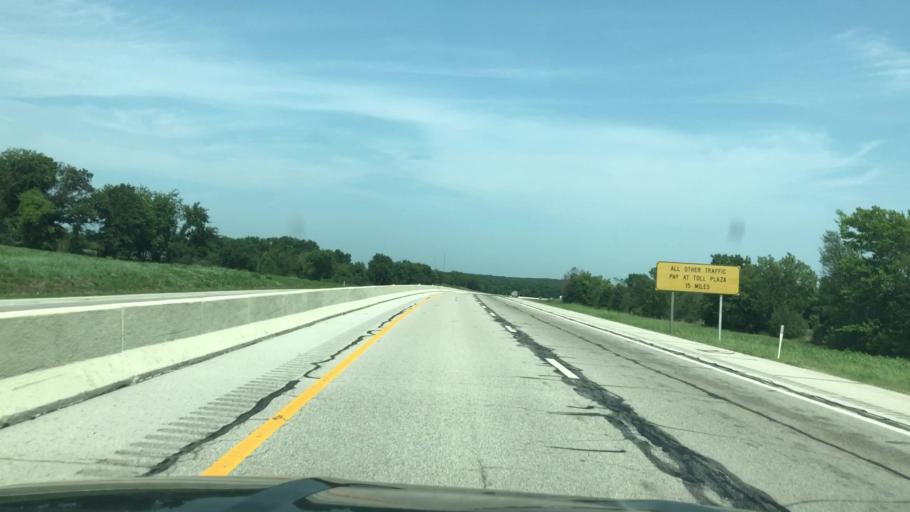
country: US
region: Oklahoma
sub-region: Rogers County
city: Chelsea
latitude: 36.4442
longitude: -95.3756
